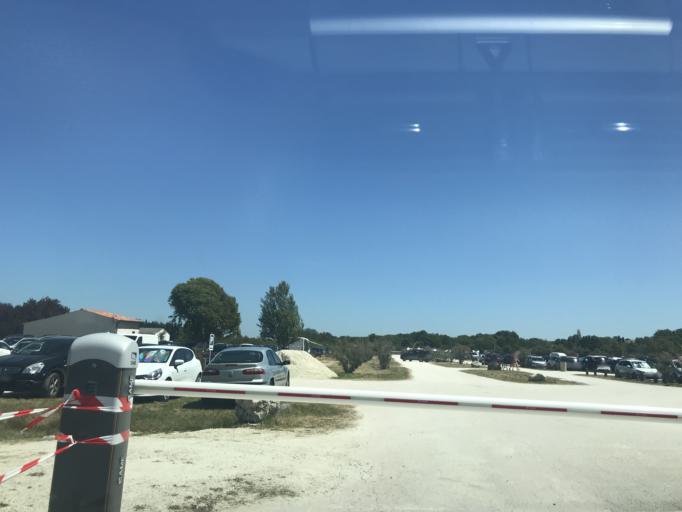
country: FR
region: Poitou-Charentes
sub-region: Departement de la Charente-Maritime
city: Meschers-sur-Gironde
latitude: 45.5373
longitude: -0.9049
